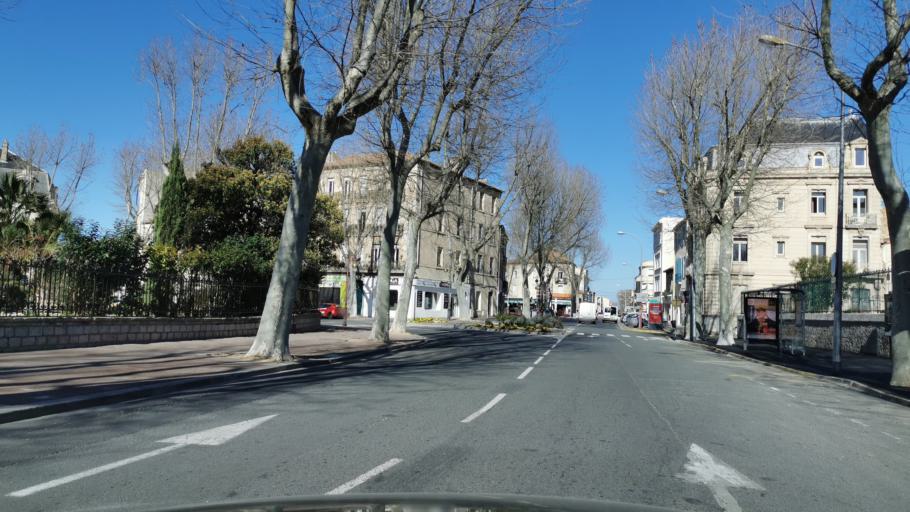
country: FR
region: Languedoc-Roussillon
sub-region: Departement de l'Aude
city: Narbonne
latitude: 43.1874
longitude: 3.0086
